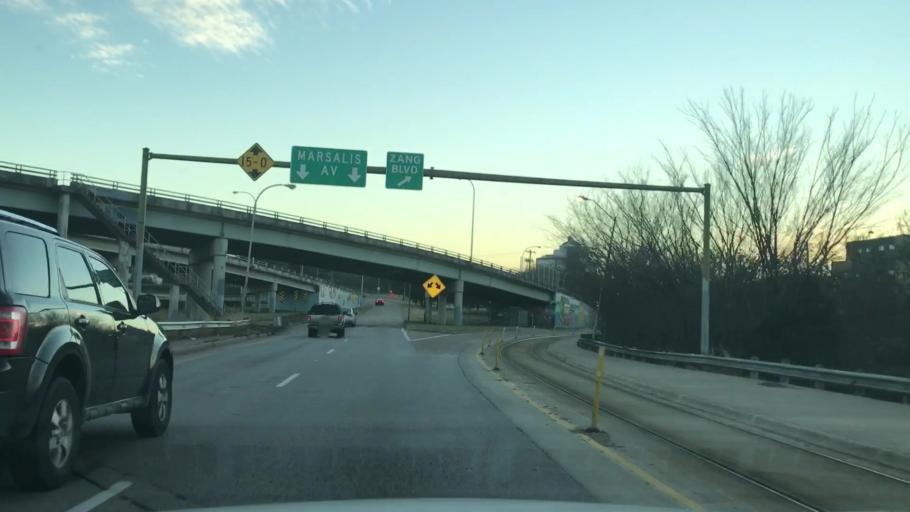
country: US
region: Texas
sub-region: Dallas County
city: Dallas
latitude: 32.7630
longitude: -96.8143
